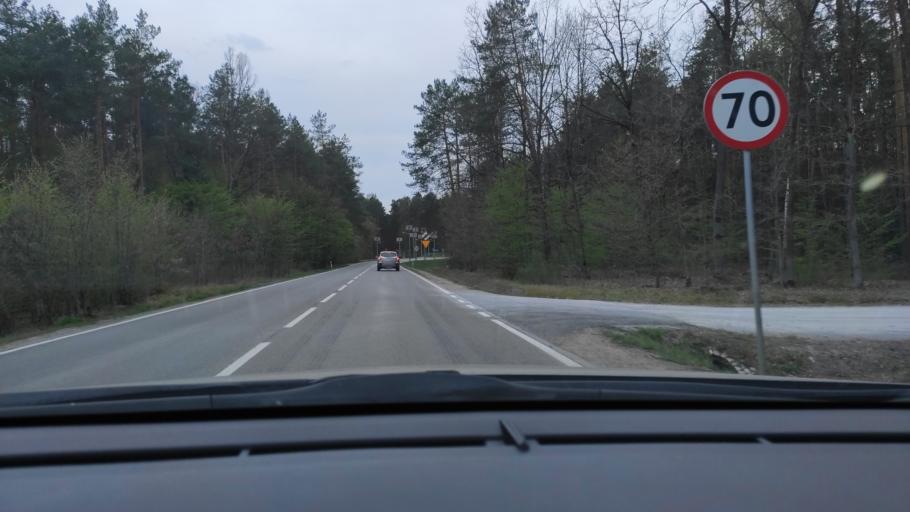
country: PL
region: Masovian Voivodeship
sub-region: Powiat radomski
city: Pionki
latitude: 51.4940
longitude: 21.4237
